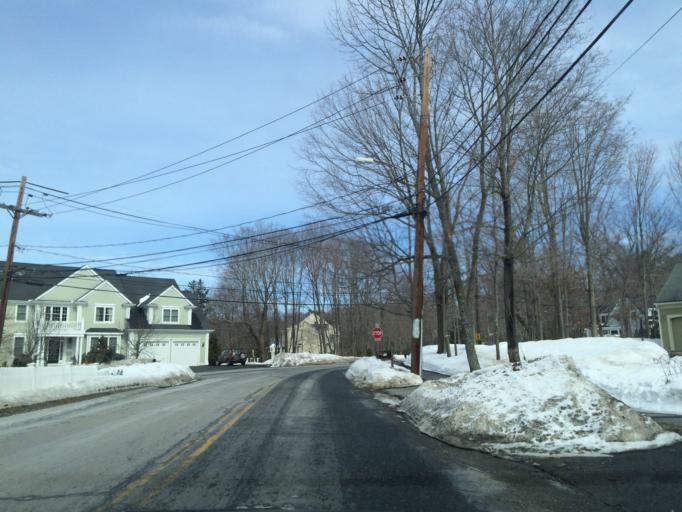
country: US
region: Massachusetts
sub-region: Middlesex County
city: Lexington
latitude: 42.4503
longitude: -71.2462
